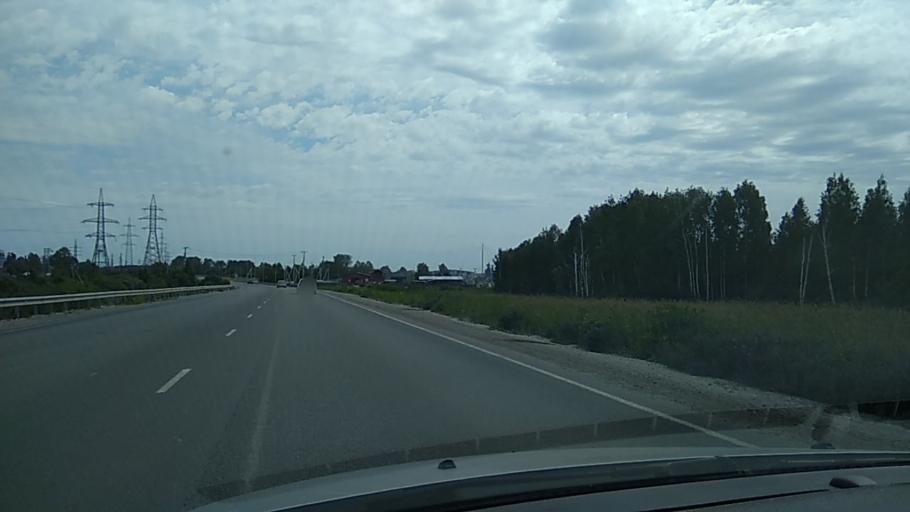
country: RU
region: Sverdlovsk
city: Verkhnyaya Pyshma
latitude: 56.9490
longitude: 60.5949
